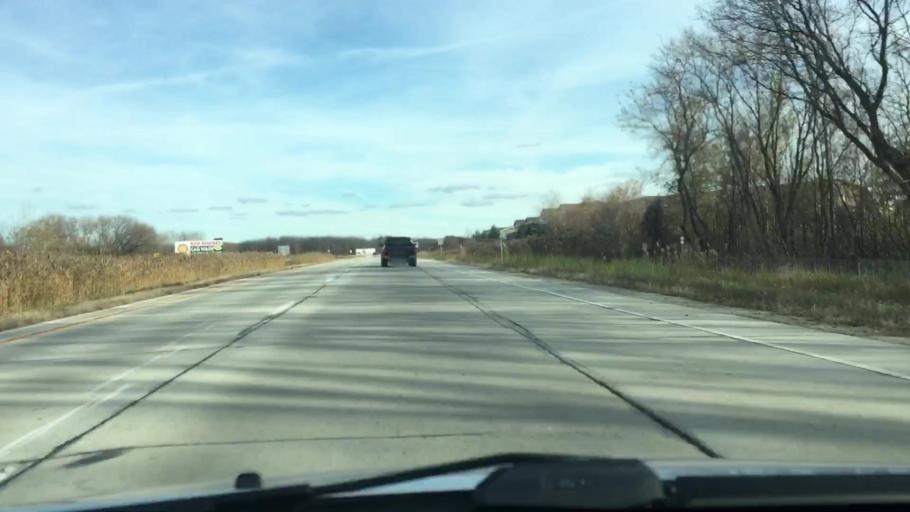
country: US
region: Wisconsin
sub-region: Brown County
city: Bellevue
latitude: 44.5241
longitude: -87.8987
